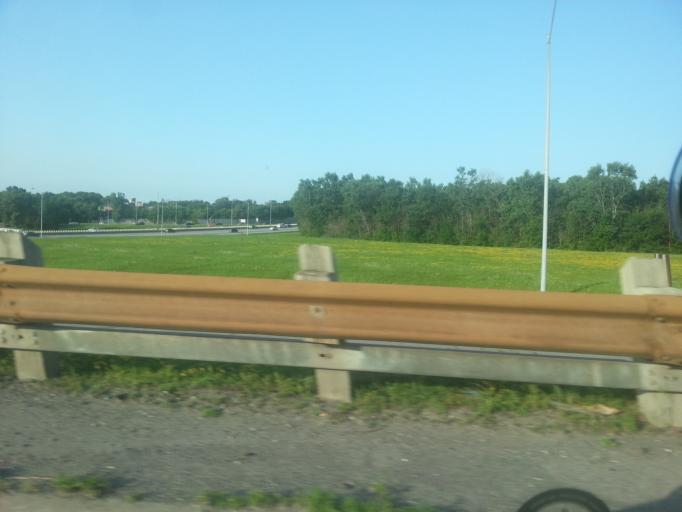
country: CA
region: Ontario
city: Ottawa
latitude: 45.4175
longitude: -75.6753
